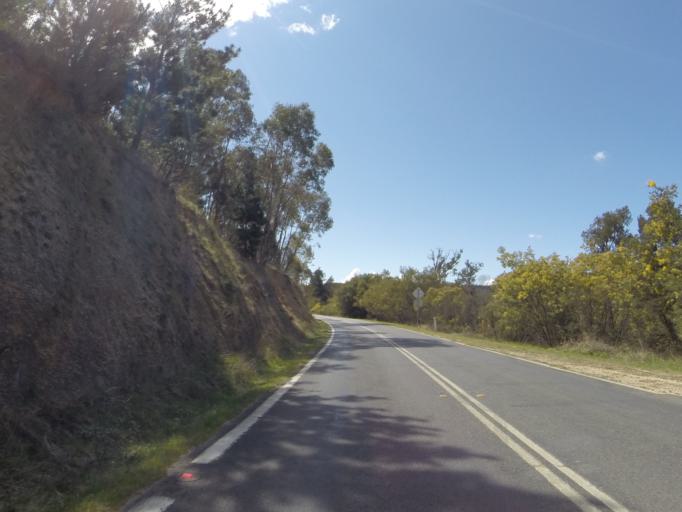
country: AU
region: Australian Capital Territory
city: Macquarie
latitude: -35.3662
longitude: 148.9514
